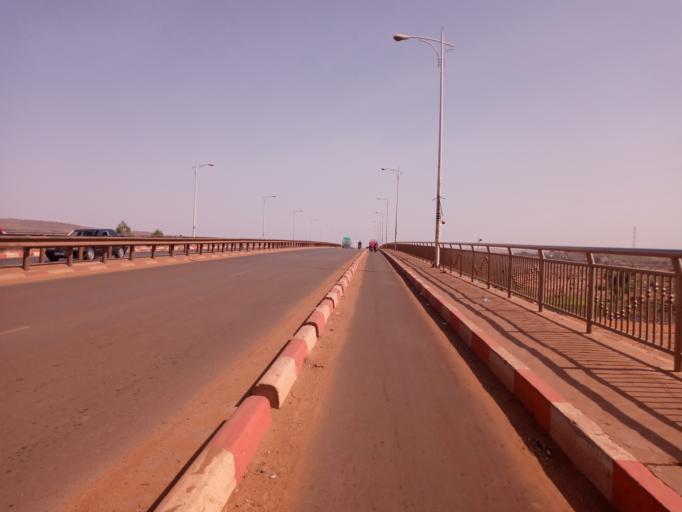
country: ML
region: Bamako
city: Bamako
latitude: 12.6493
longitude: -7.9296
